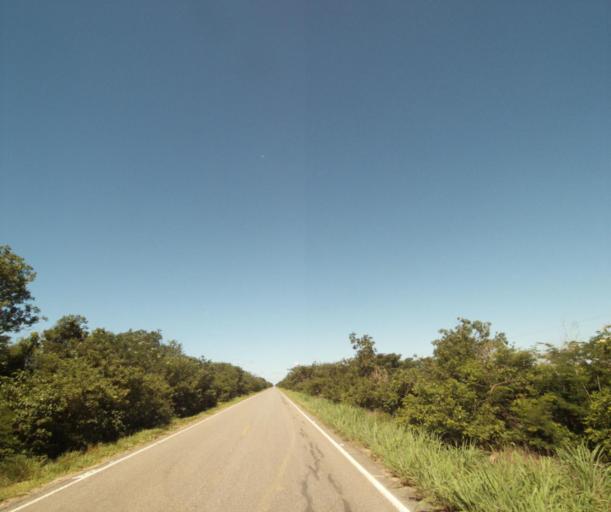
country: BR
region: Bahia
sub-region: Carinhanha
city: Carinhanha
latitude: -14.2827
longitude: -43.5613
